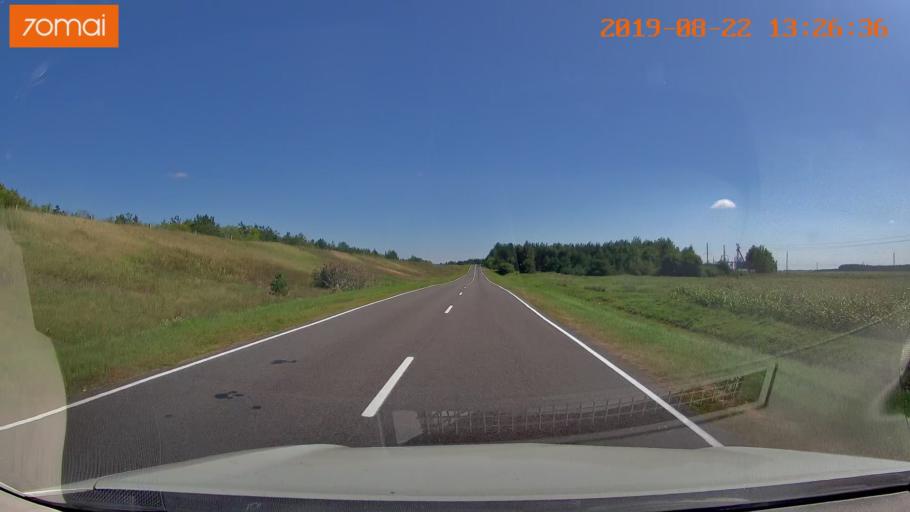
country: BY
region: Minsk
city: Staryya Darohi
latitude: 53.2088
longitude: 28.0659
